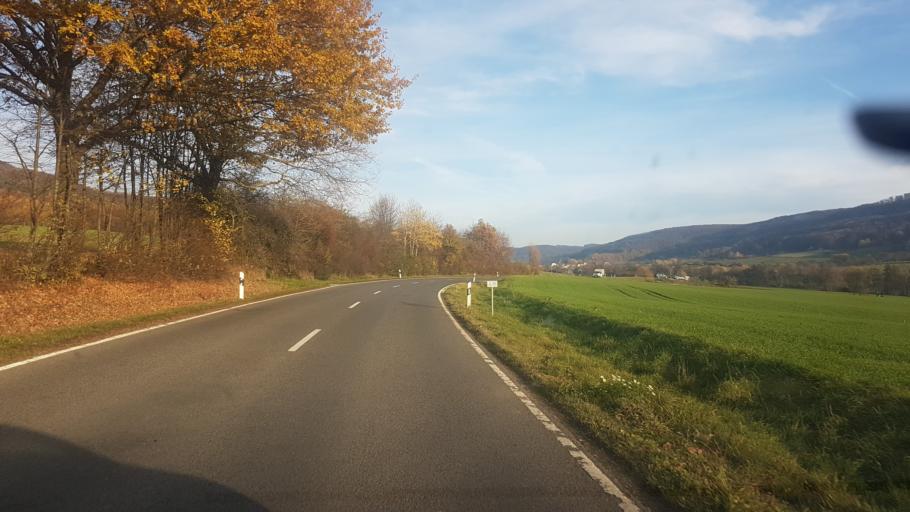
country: DE
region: Bavaria
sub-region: Upper Franconia
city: Litzendorf
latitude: 49.9155
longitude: 11.0213
